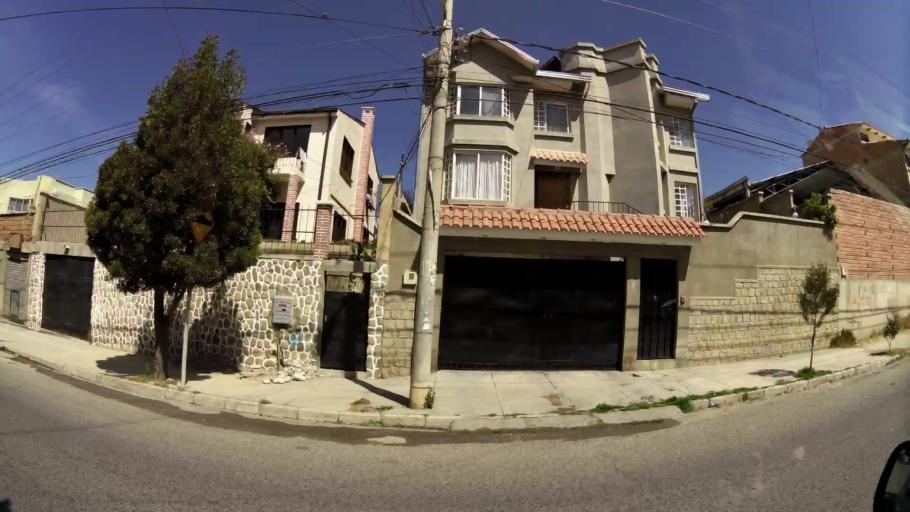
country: BO
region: La Paz
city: La Paz
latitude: -16.5332
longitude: -68.1037
